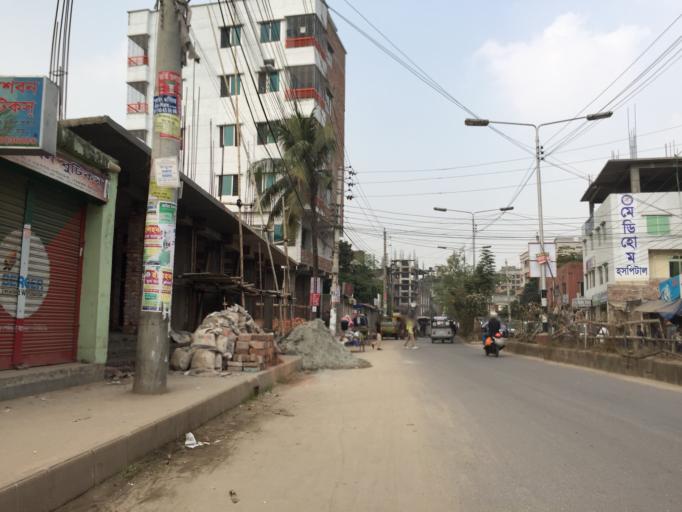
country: BD
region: Dhaka
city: Azimpur
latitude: 23.7906
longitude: 90.3661
